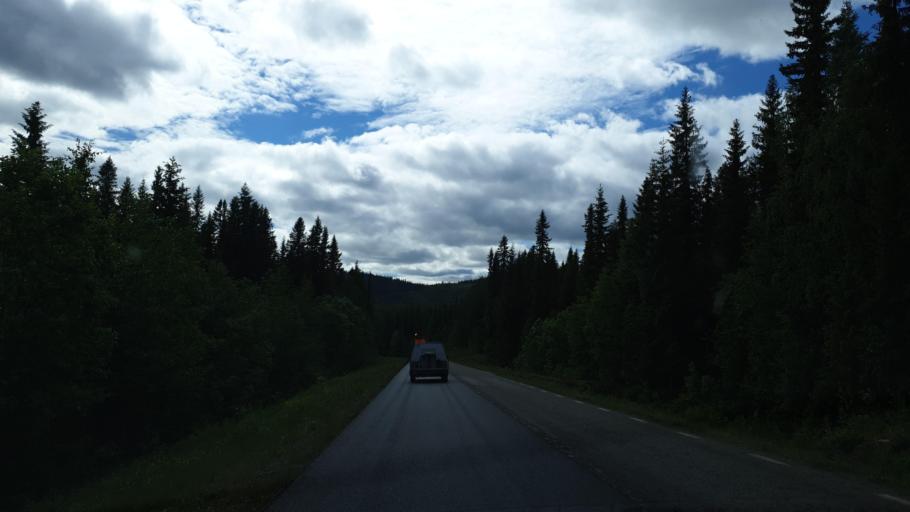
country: SE
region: Vaesterbotten
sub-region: Vilhelmina Kommun
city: Sjoberg
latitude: 64.9074
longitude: 15.8662
